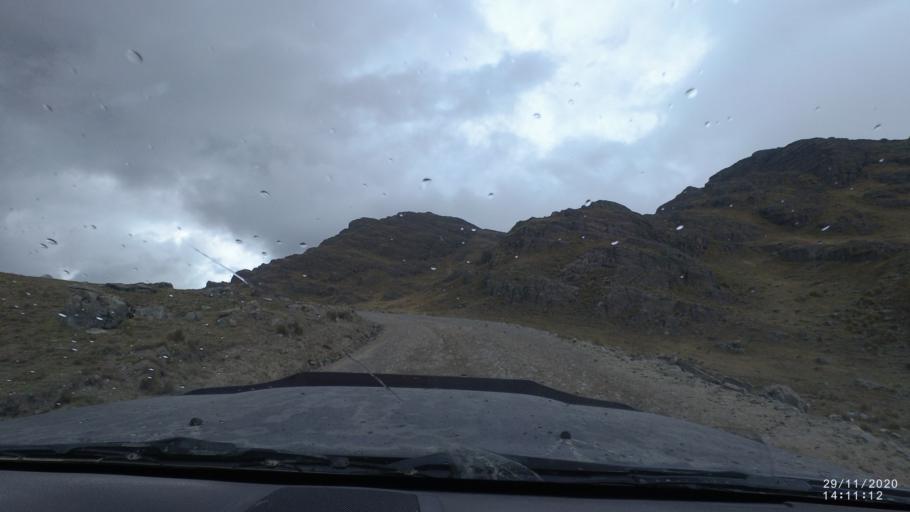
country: BO
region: Cochabamba
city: Sipe Sipe
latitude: -17.2330
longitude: -66.3921
